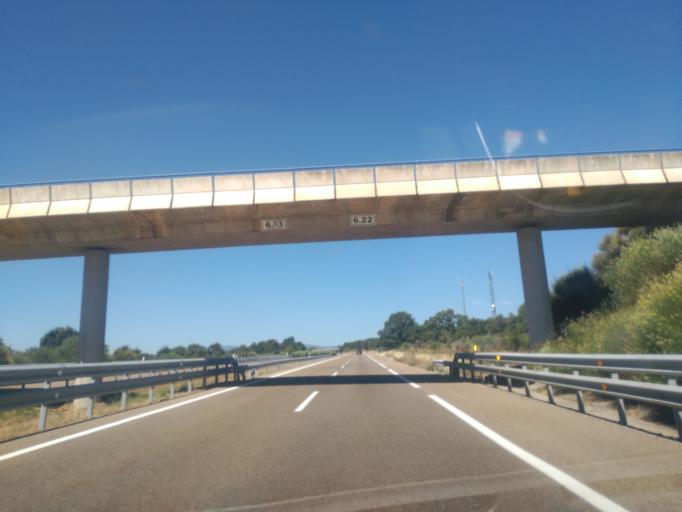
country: ES
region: Castille and Leon
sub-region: Provincia de Zamora
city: Asturianos
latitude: 42.0409
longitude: -6.4625
